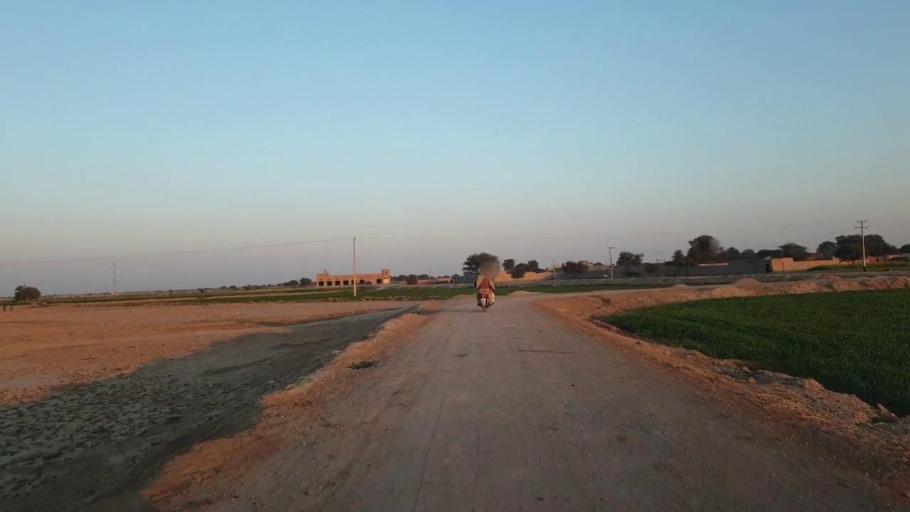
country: PK
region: Sindh
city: Shahpur Chakar
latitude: 26.1662
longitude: 68.5449
